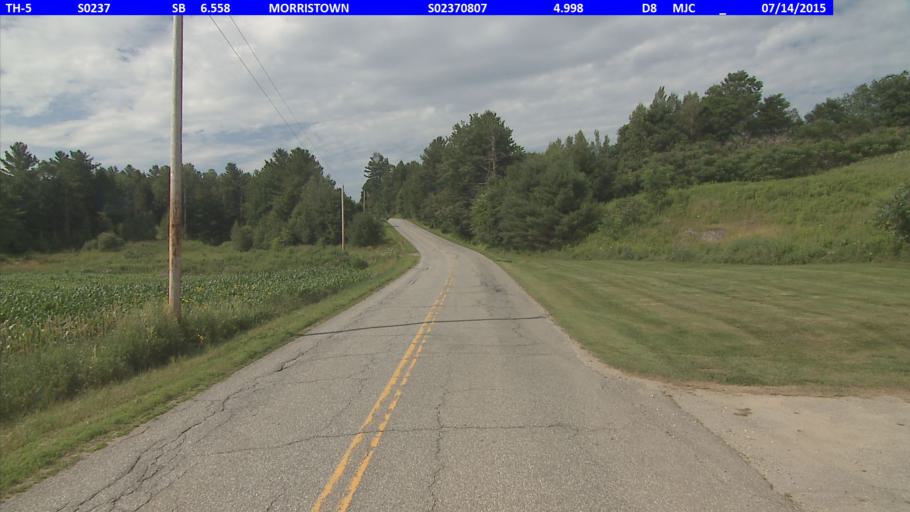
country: US
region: Vermont
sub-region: Lamoille County
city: Morristown
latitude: 44.5671
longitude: -72.6197
